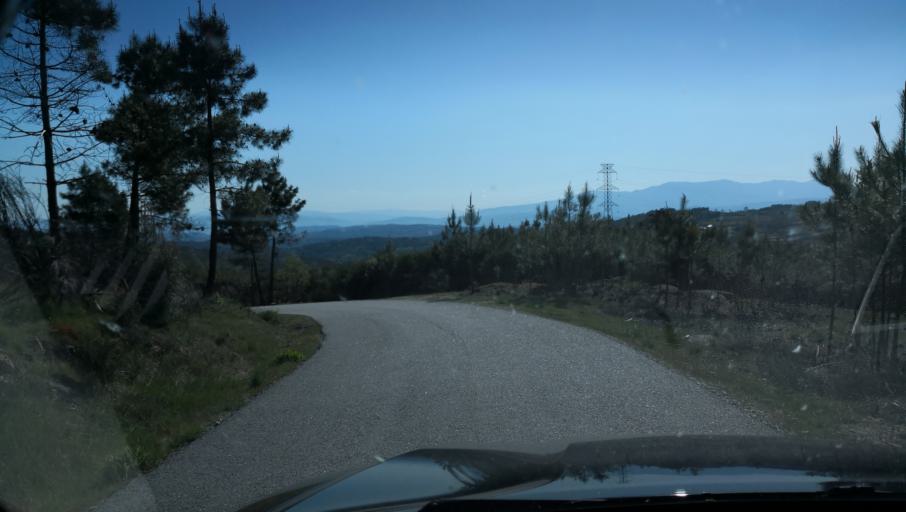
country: PT
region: Vila Real
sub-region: Sabrosa
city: Sabrosa
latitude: 41.2961
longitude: -7.6355
